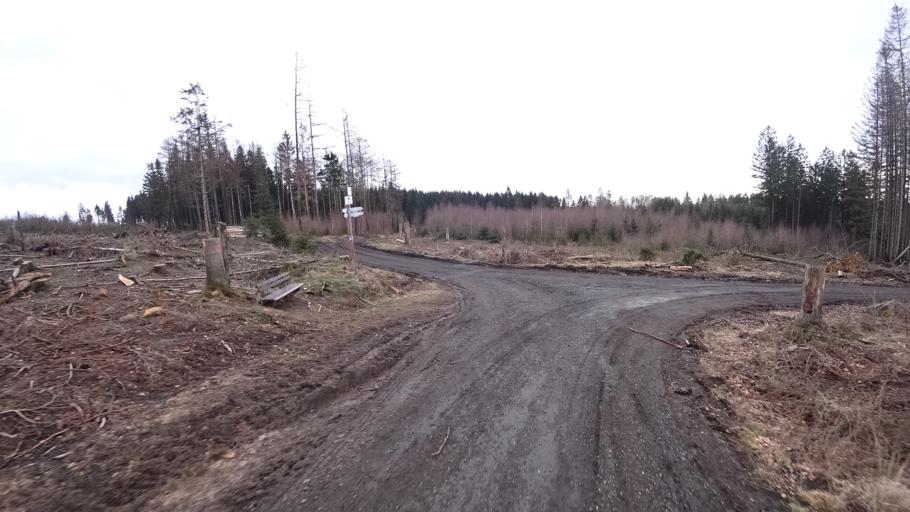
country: DE
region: Rheinland-Pfalz
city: Hillscheid
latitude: 50.4232
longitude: 7.7278
